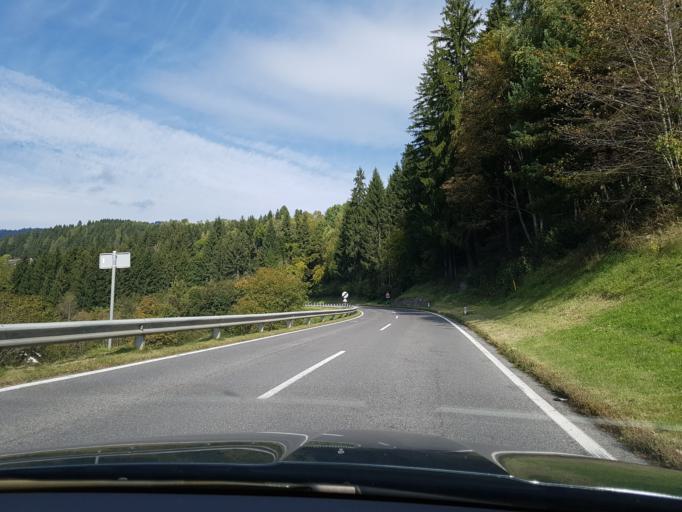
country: AT
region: Carinthia
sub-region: Politischer Bezirk Feldkirchen
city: Himmelberg
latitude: 46.7595
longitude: 14.0237
